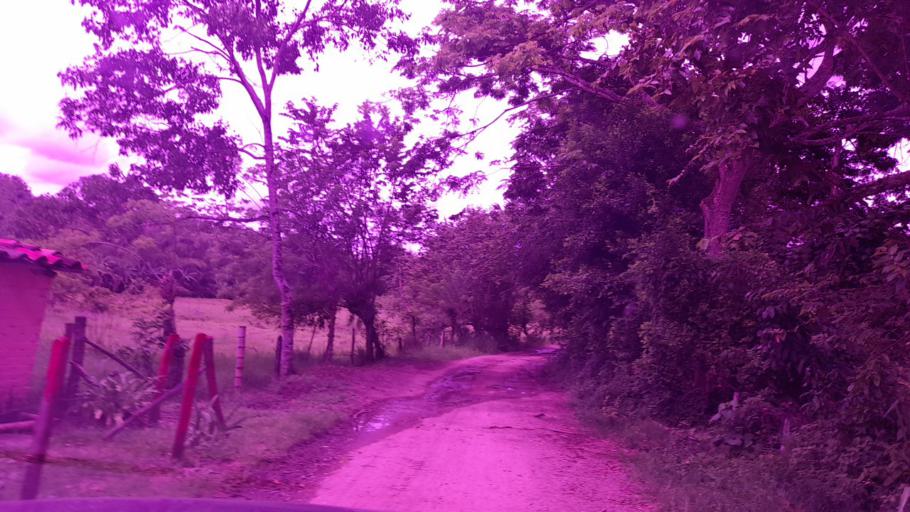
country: CO
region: Valle del Cauca
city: Andalucia
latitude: 4.1666
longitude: -76.0896
